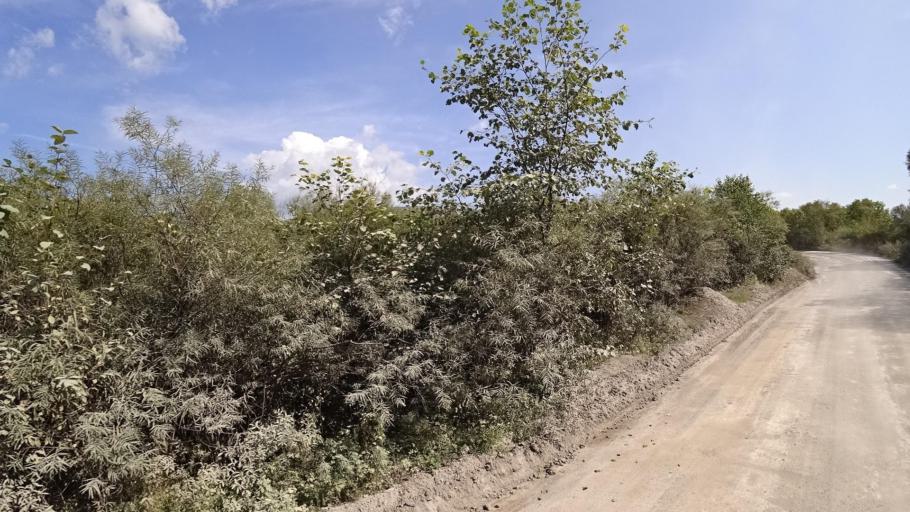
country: RU
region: Jewish Autonomous Oblast
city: Londoko
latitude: 49.0225
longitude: 131.9282
